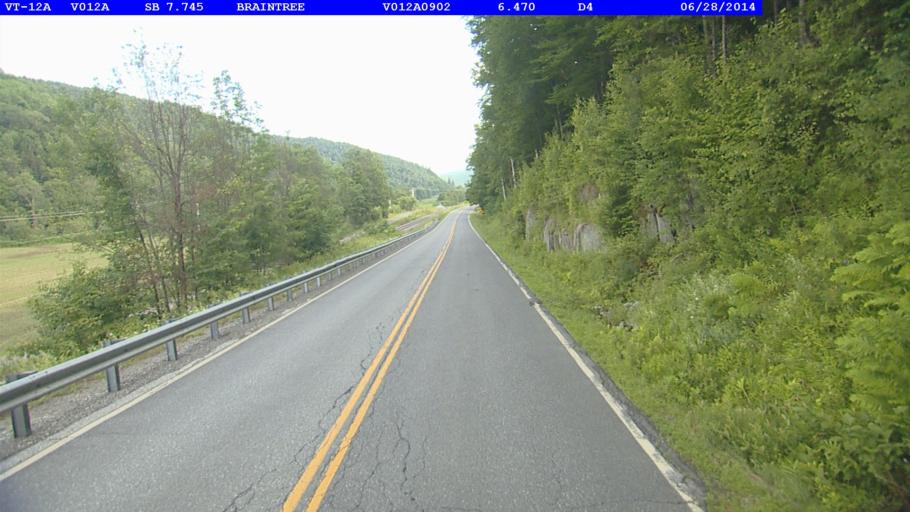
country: US
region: Vermont
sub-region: Orange County
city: Randolph
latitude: 44.0004
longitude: -72.7530
